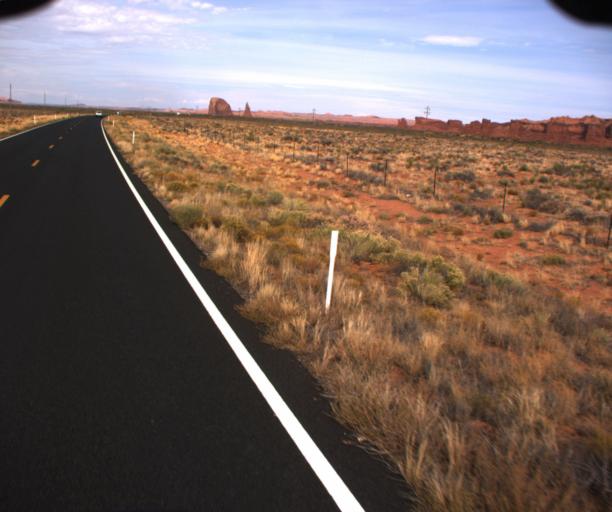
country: US
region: Arizona
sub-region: Apache County
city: Many Farms
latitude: 36.6158
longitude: -109.5797
